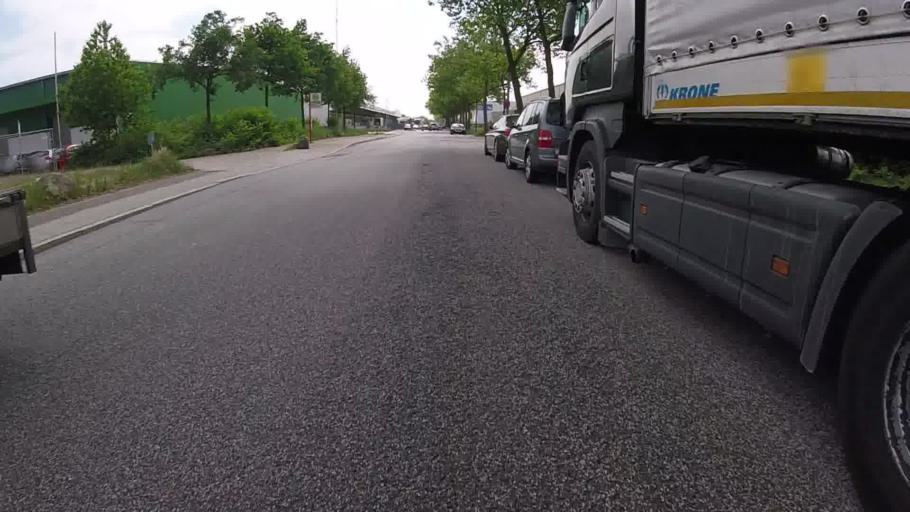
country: DE
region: Hamburg
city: Marienthal
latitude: 53.5228
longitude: 10.0877
